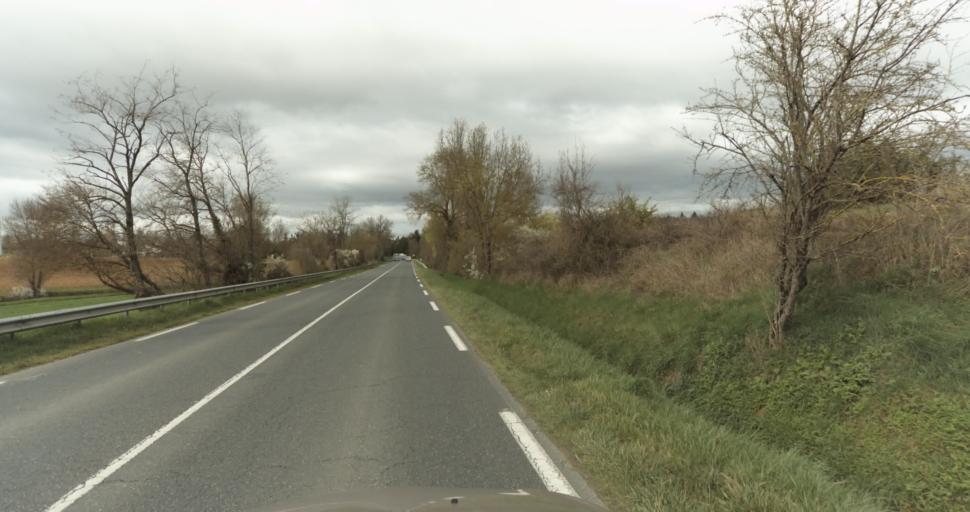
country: FR
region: Midi-Pyrenees
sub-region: Departement du Tarn
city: Puygouzon
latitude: 43.8854
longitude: 2.1673
